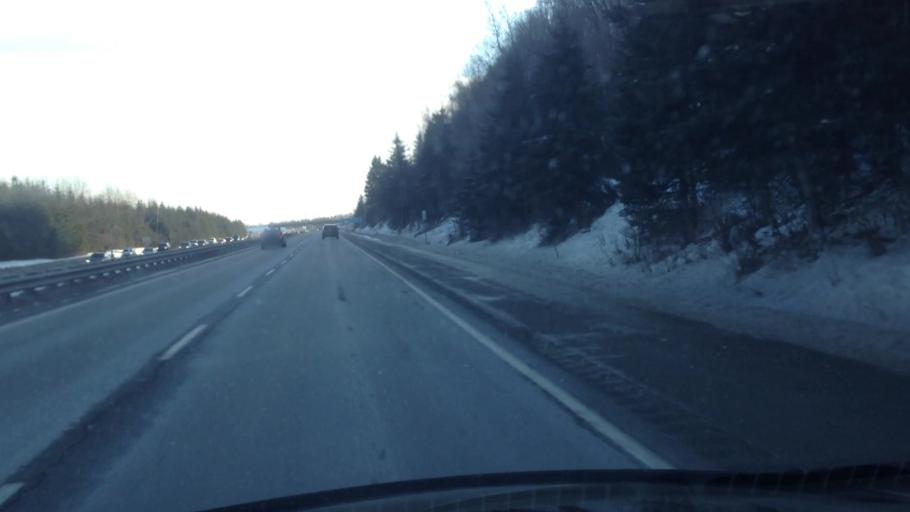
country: CA
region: Quebec
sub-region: Laurentides
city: Prevost
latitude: 45.8495
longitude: -74.0739
